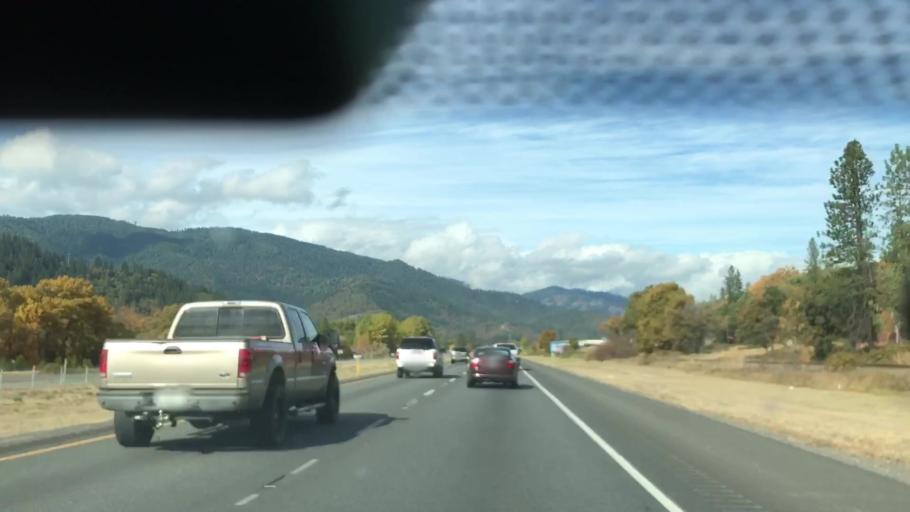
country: US
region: Oregon
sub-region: Jackson County
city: Rogue River
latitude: 42.4170
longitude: -123.1574
